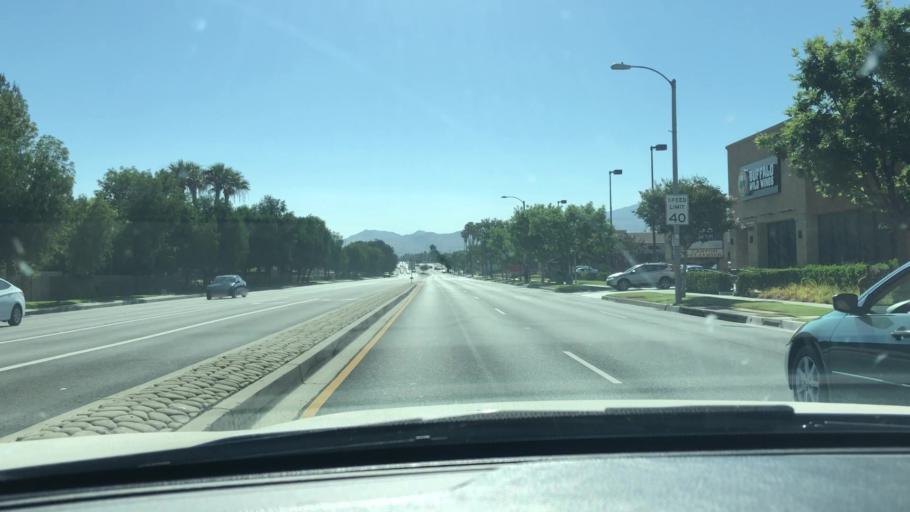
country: US
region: California
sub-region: Los Angeles County
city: Santa Clarita
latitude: 34.4157
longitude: -118.4717
